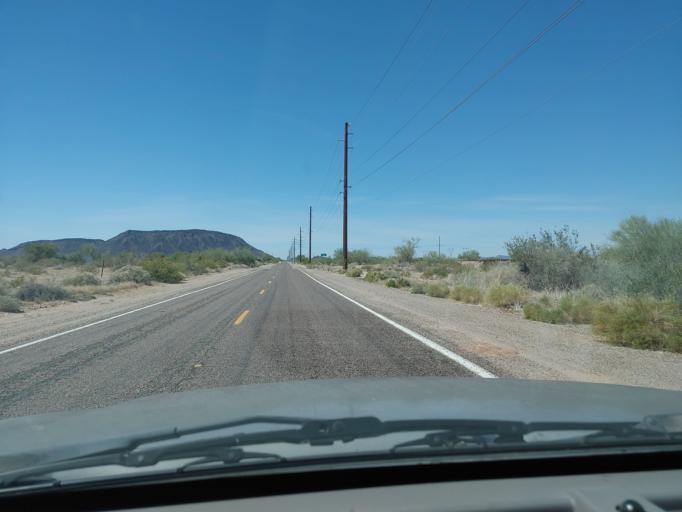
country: US
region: Arizona
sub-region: Maricopa County
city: Gila Bend
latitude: 33.0298
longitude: -113.3203
